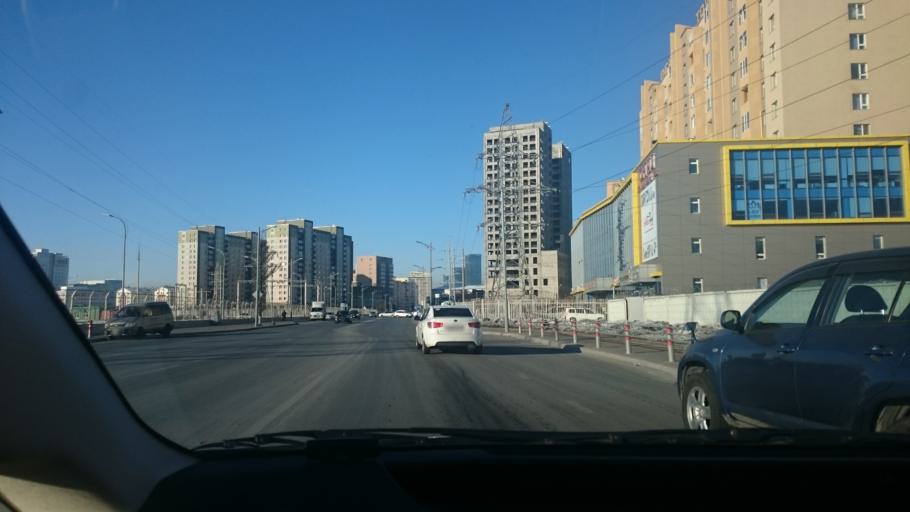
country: MN
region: Ulaanbaatar
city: Ulaanbaatar
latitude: 47.9002
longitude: 106.9306
